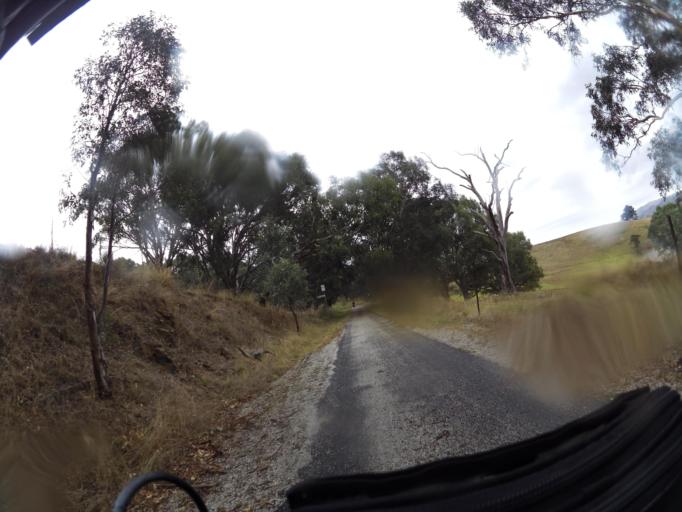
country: AU
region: New South Wales
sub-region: Albury Municipality
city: East Albury
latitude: -36.2159
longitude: 147.2370
